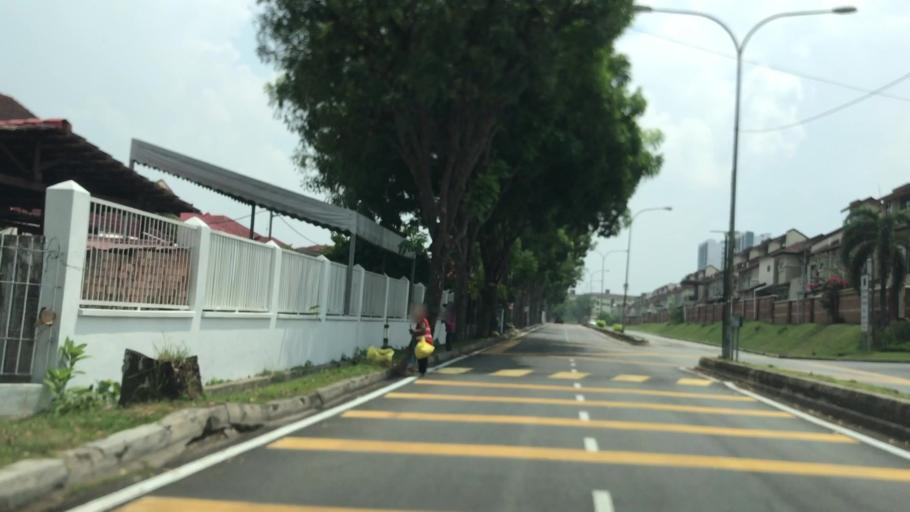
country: MY
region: Selangor
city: Subang Jaya
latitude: 3.0018
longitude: 101.6256
